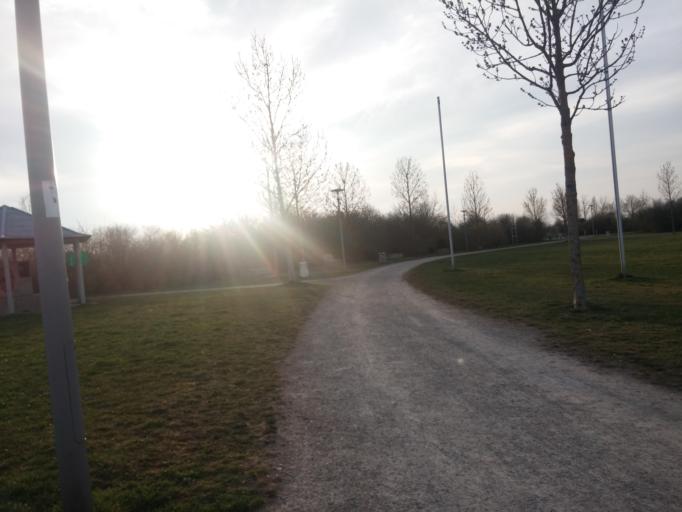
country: DE
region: Bavaria
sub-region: Upper Bavaria
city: Aschheim
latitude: 48.1632
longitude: 11.7134
